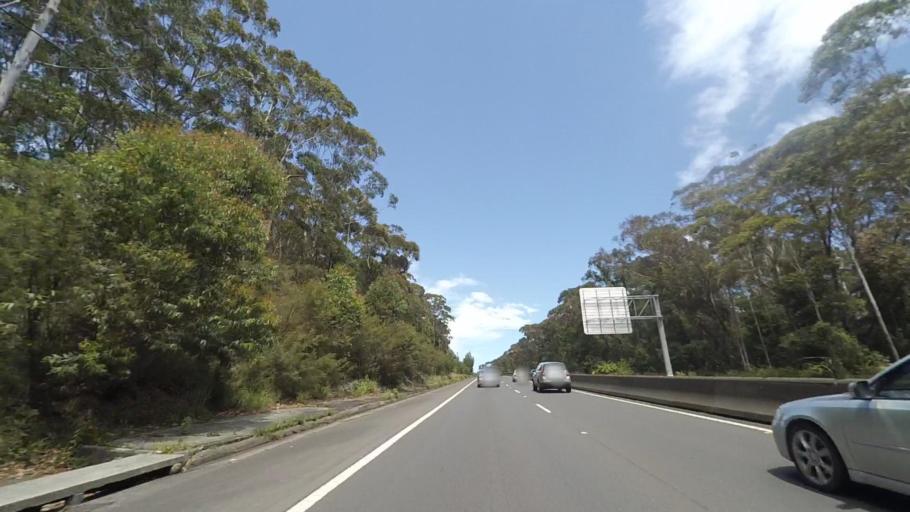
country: AU
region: New South Wales
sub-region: Wollongong
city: Bulli
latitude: -34.3170
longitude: 150.8919
